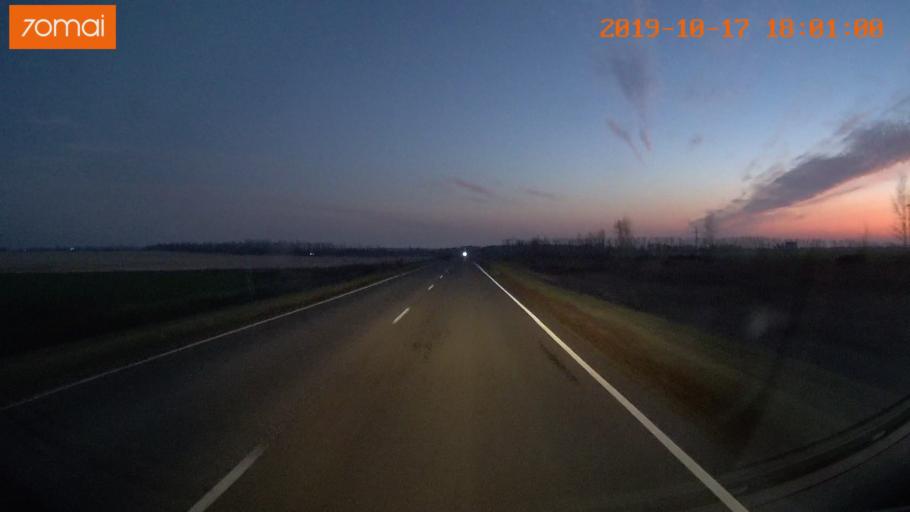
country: RU
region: Tula
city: Kurkino
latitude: 53.5139
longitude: 38.6126
